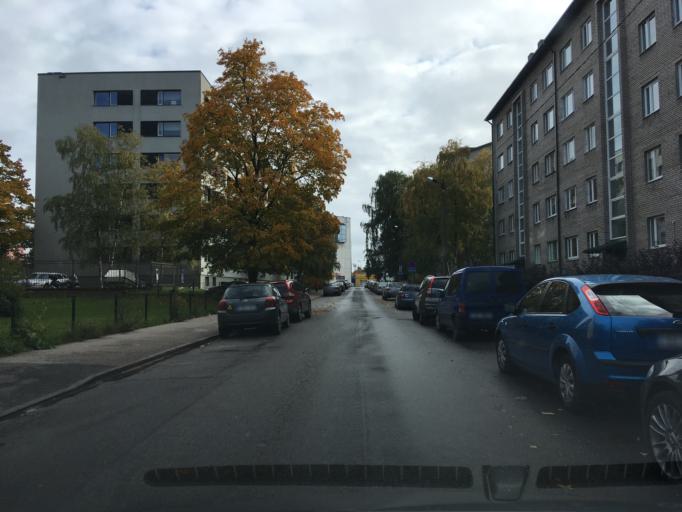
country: EE
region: Harju
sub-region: Tallinna linn
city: Tallinn
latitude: 59.4308
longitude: 24.7894
